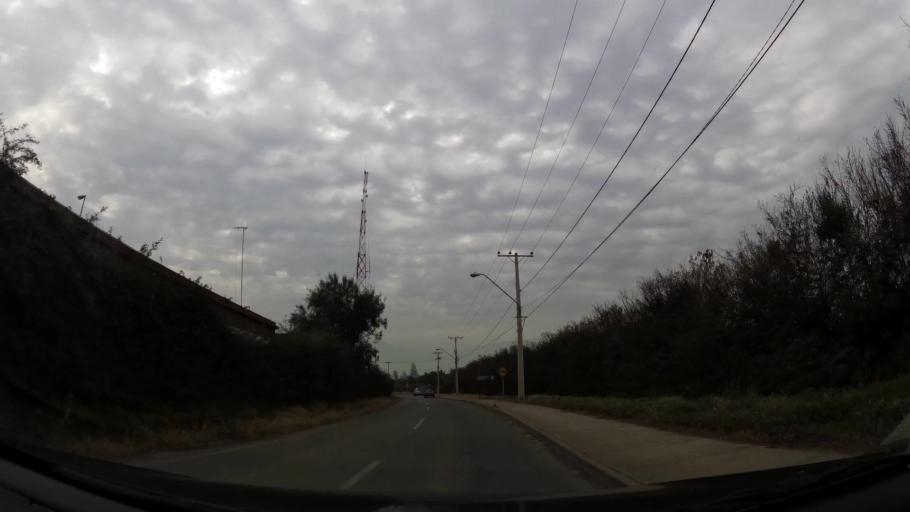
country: CL
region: Santiago Metropolitan
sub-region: Provincia de Chacabuco
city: Chicureo Abajo
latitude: -33.2336
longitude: -70.6923
